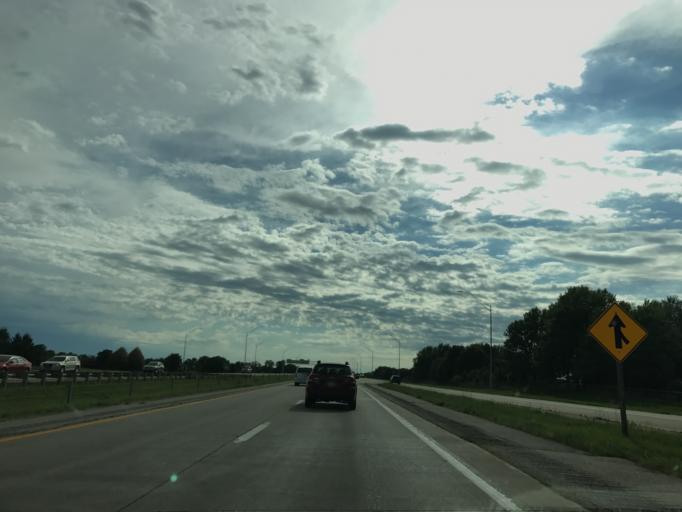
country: US
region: Iowa
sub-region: Dallas County
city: Waukee
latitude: 41.5910
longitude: -93.8116
